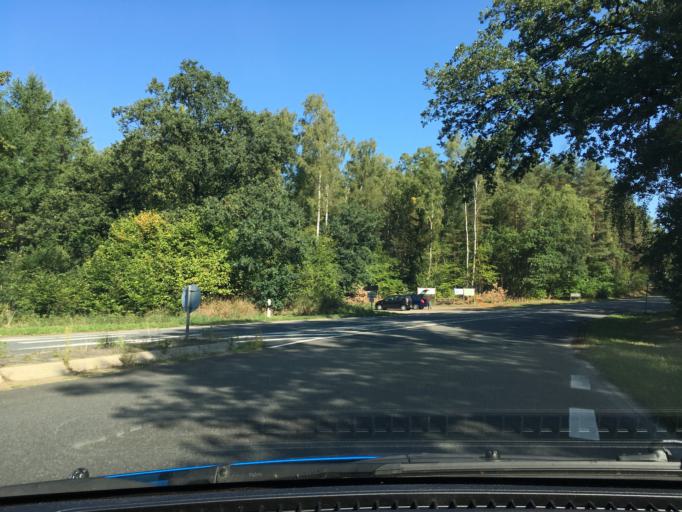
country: DE
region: Lower Saxony
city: Munster
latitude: 52.9553
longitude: 10.1281
